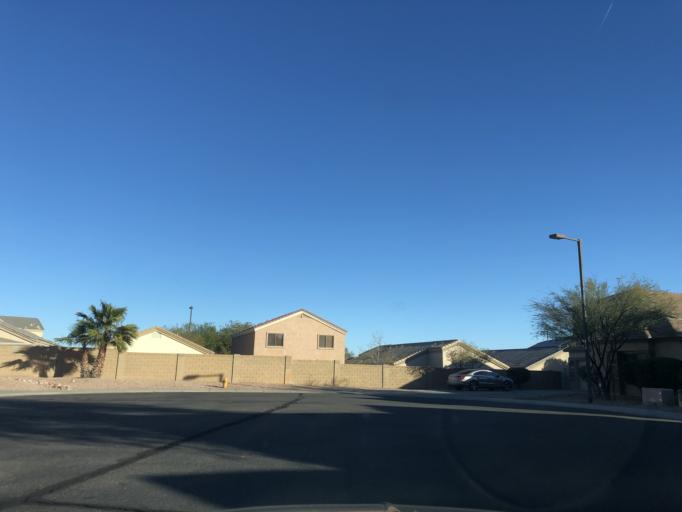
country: US
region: Arizona
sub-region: Maricopa County
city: Buckeye
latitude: 33.4387
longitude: -112.5676
